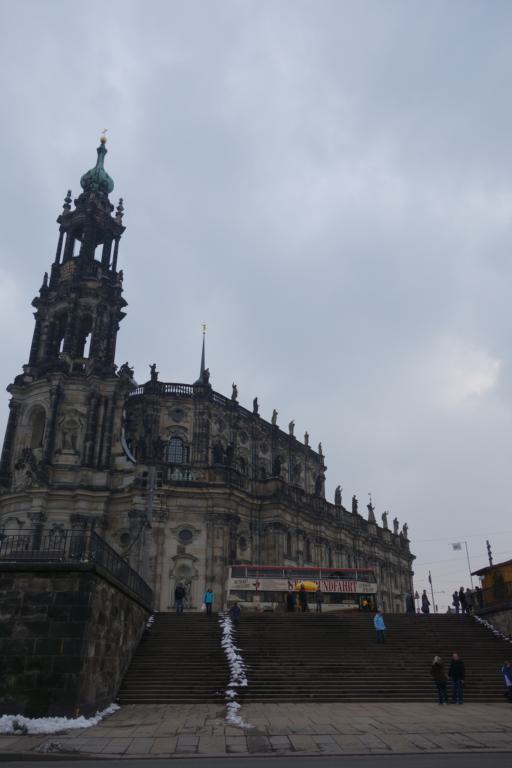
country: DE
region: Saxony
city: Dresden
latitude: 51.0544
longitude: 13.7381
